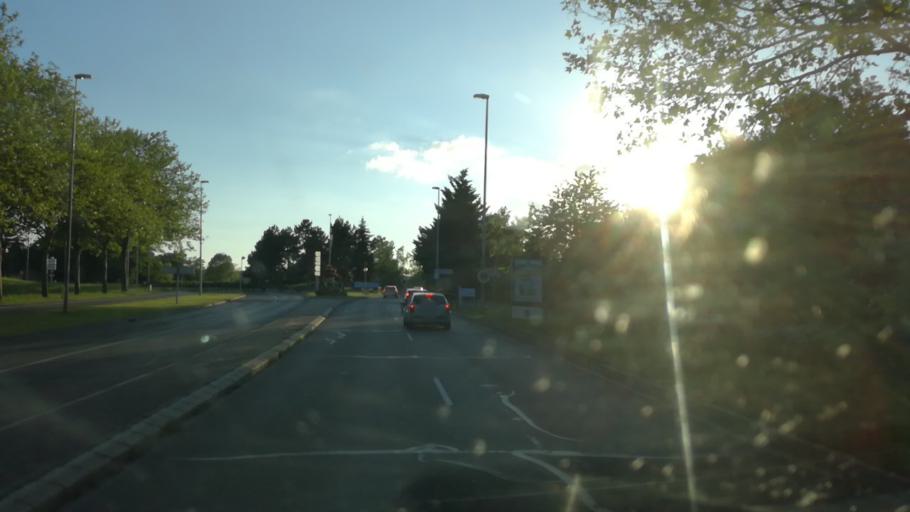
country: FR
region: Ile-de-France
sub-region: Departement des Yvelines
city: Elancourt
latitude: 48.7782
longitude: 1.9610
